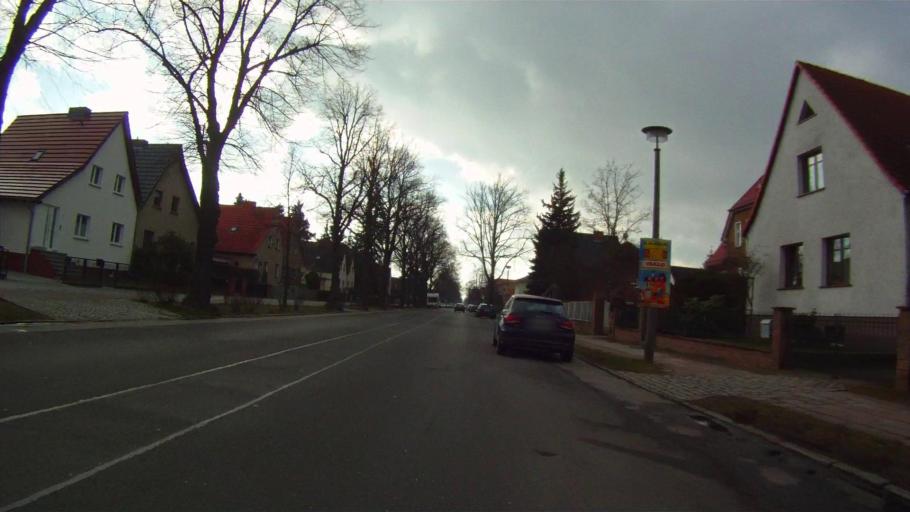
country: DE
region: Berlin
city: Biesdorf
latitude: 52.5222
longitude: 13.5564
